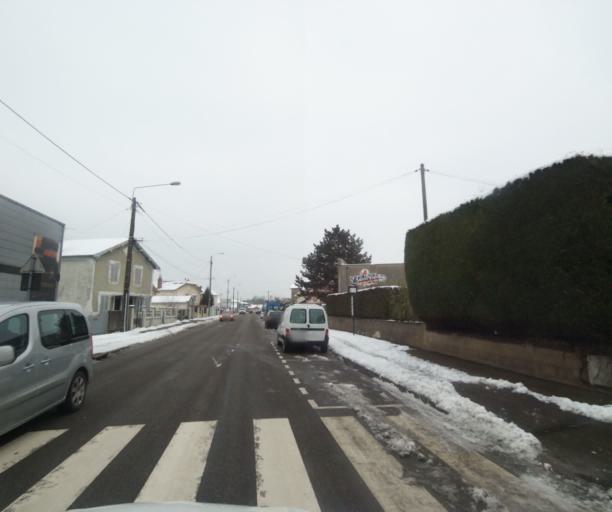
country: FR
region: Champagne-Ardenne
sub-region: Departement de la Haute-Marne
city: Saint-Dizier
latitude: 48.6307
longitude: 4.9343
